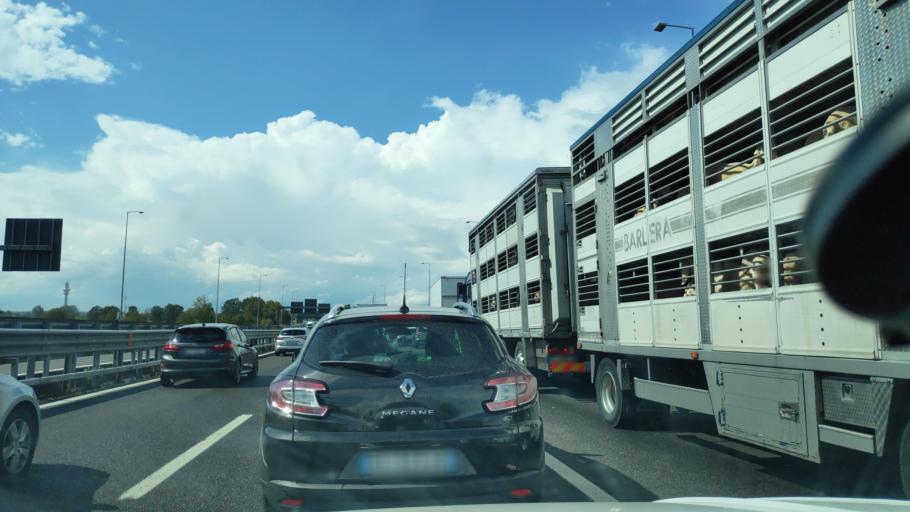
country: IT
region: Lombardy
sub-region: Citta metropolitana di Milano
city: Noverasco-Sporting Mirasole
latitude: 45.3915
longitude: 9.2078
